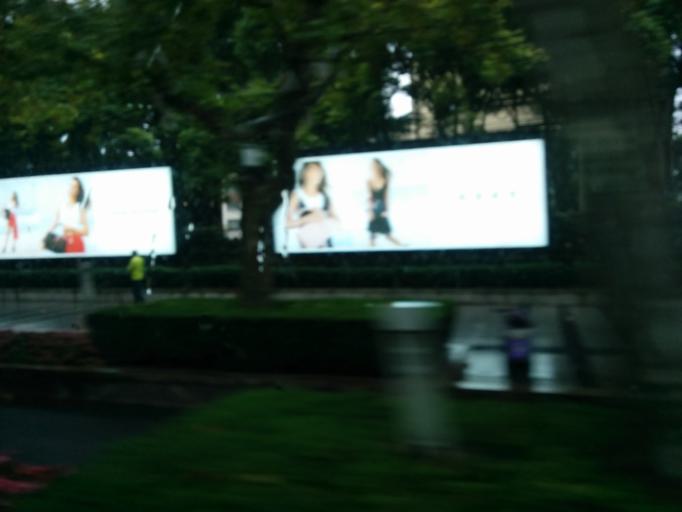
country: CN
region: Shanghai Shi
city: Shanghai
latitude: 31.2273
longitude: 121.4464
